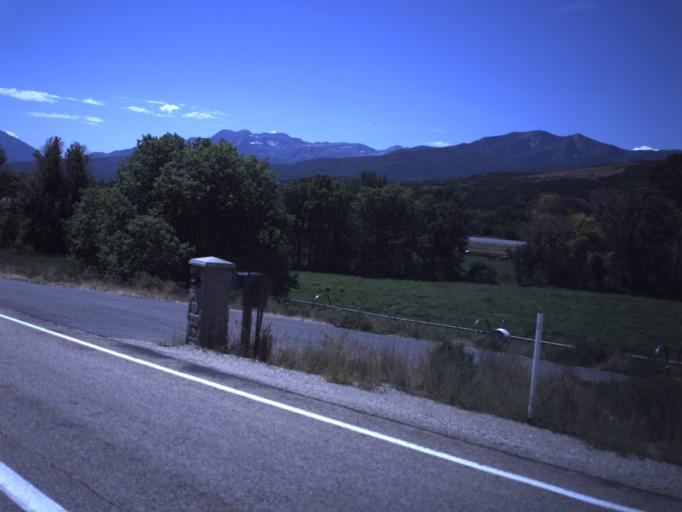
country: US
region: Utah
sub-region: Wasatch County
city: Heber
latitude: 40.5616
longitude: -111.4244
